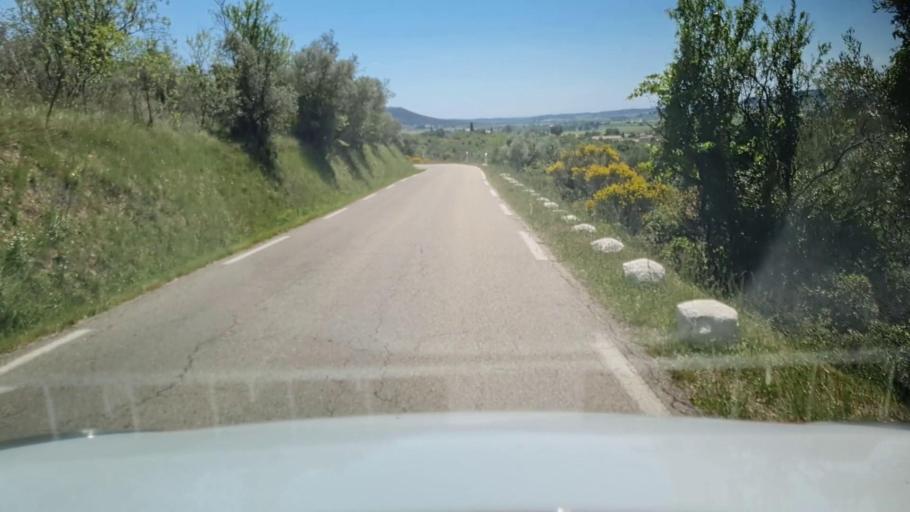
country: FR
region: Languedoc-Roussillon
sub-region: Departement du Gard
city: Clarensac
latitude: 43.8363
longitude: 4.2164
